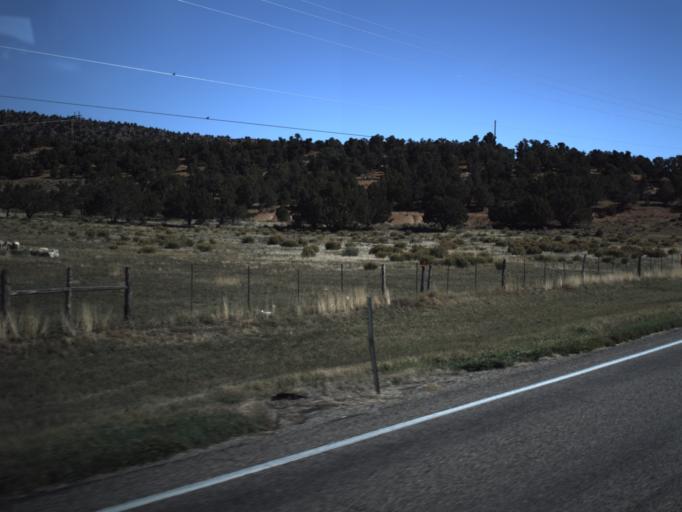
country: US
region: Utah
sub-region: Iron County
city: Cedar City
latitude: 37.6326
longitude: -113.2956
